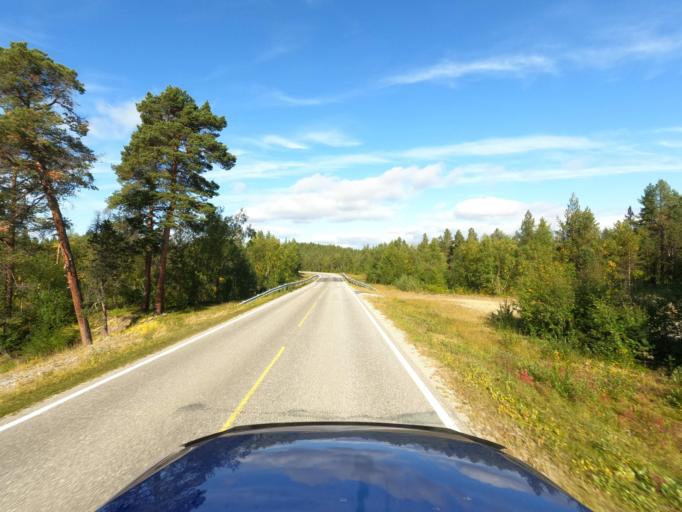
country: NO
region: Finnmark Fylke
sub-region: Porsanger
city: Lakselv
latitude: 69.8196
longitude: 25.1568
